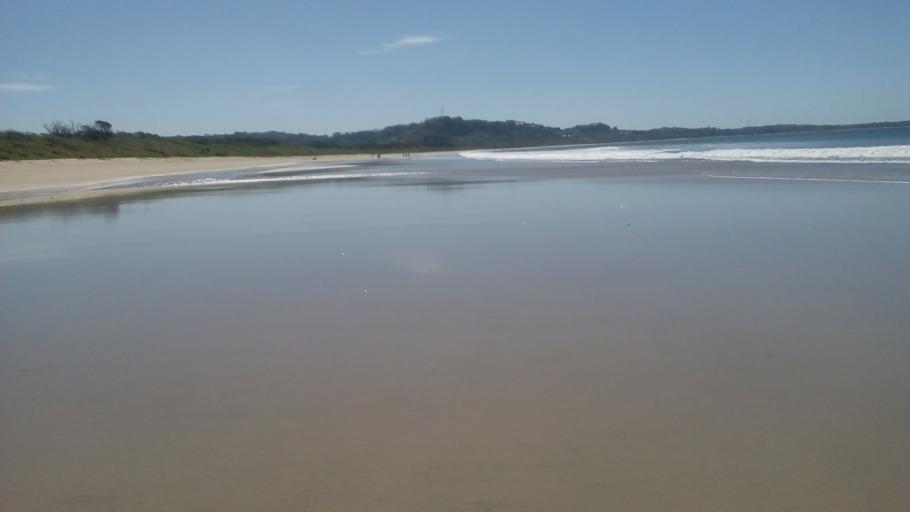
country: CR
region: Guanacaste
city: Belen
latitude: 10.3304
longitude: -85.8462
